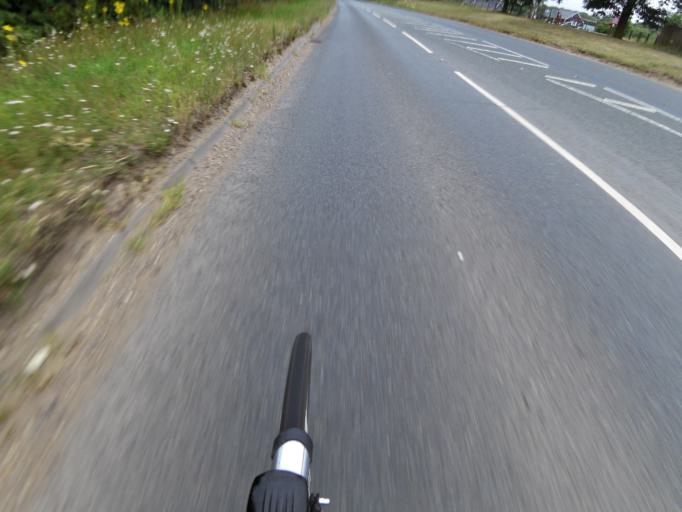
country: GB
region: England
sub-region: Suffolk
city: Bramford
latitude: 52.0908
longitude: 1.0913
